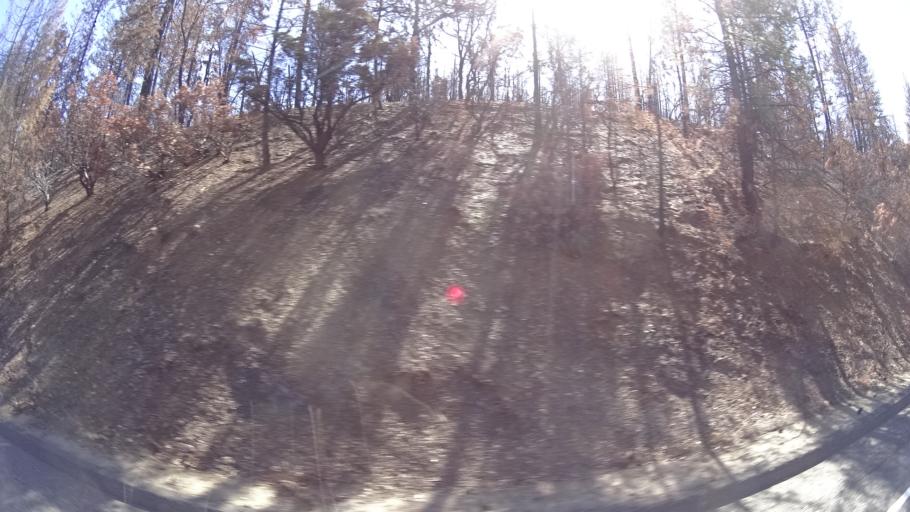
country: US
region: California
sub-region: Tehama County
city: Rancho Tehama Reserve
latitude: 39.6713
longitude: -122.7123
